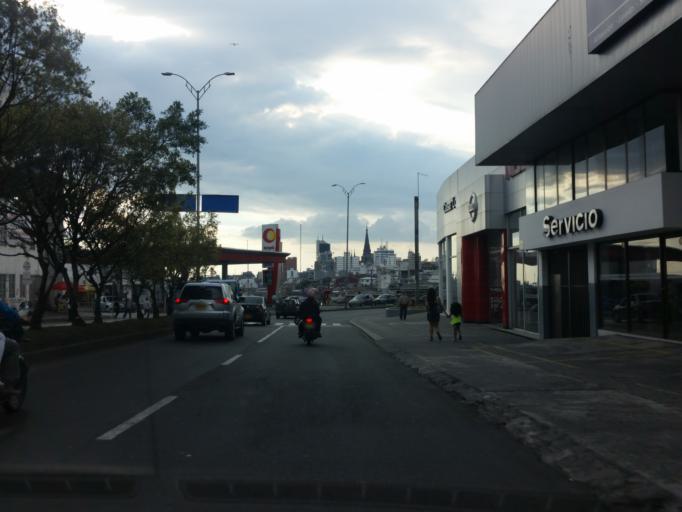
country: CO
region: Caldas
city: Manizales
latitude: 5.0661
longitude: -75.5061
